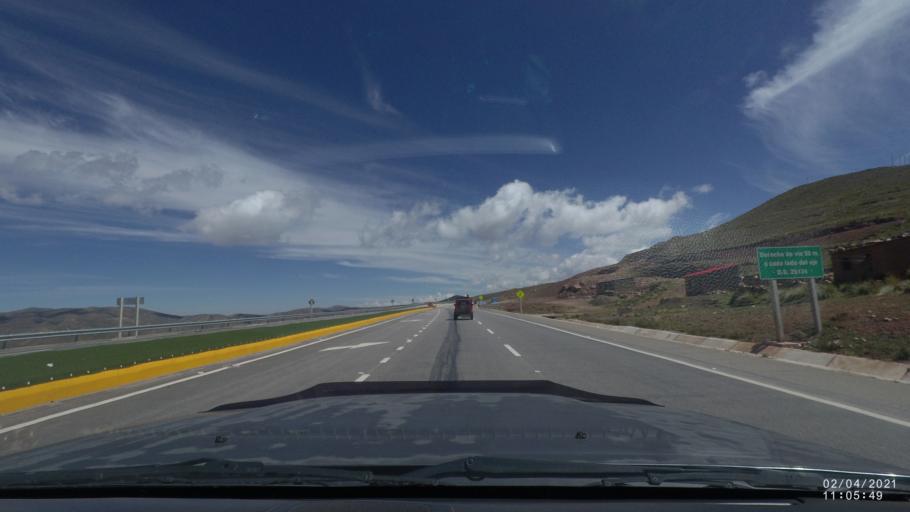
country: BO
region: Cochabamba
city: Colchani
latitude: -17.6553
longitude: -66.8325
